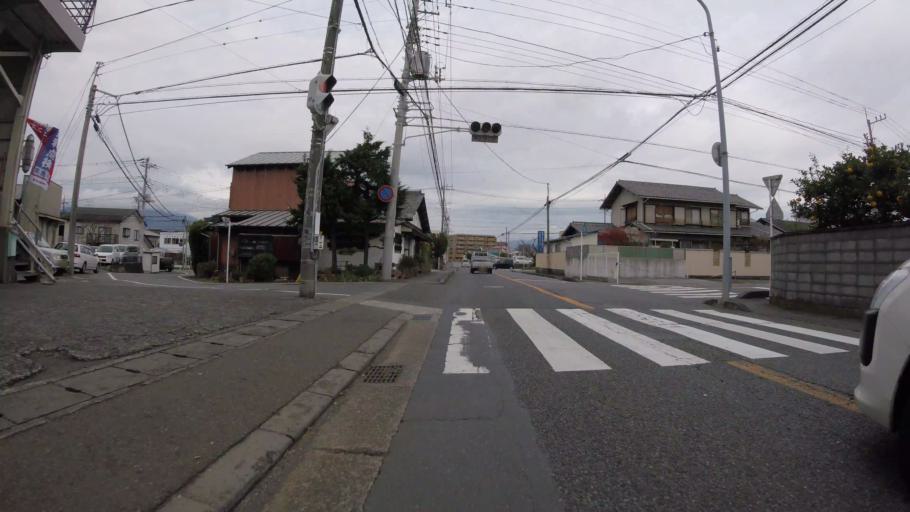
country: JP
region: Shizuoka
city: Numazu
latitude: 35.1028
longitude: 138.8914
